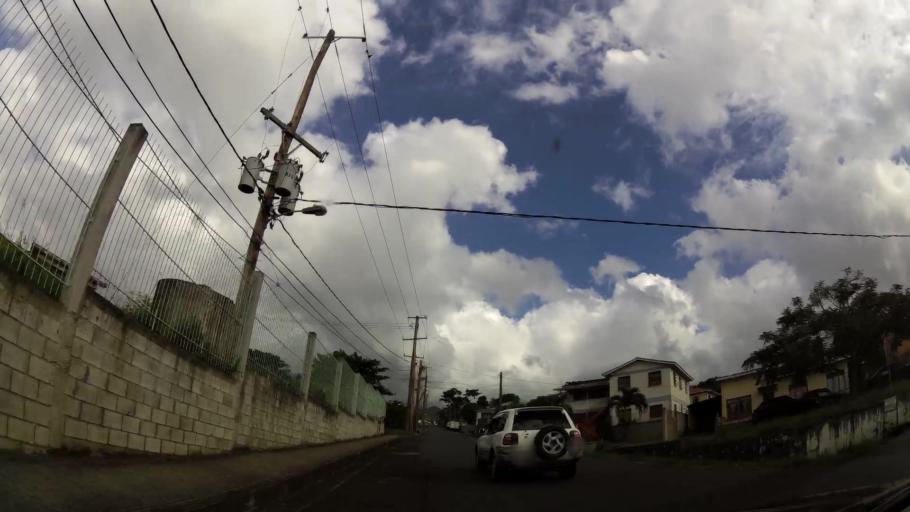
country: DM
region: Saint George
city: Roseau
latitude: 15.3057
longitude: -61.3834
